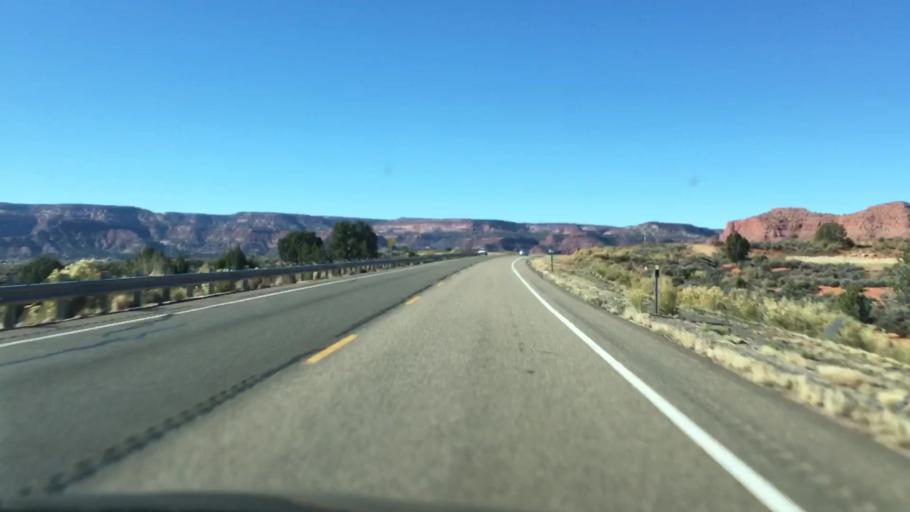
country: US
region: Utah
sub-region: Kane County
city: Kanab
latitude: 37.0306
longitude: -112.4903
